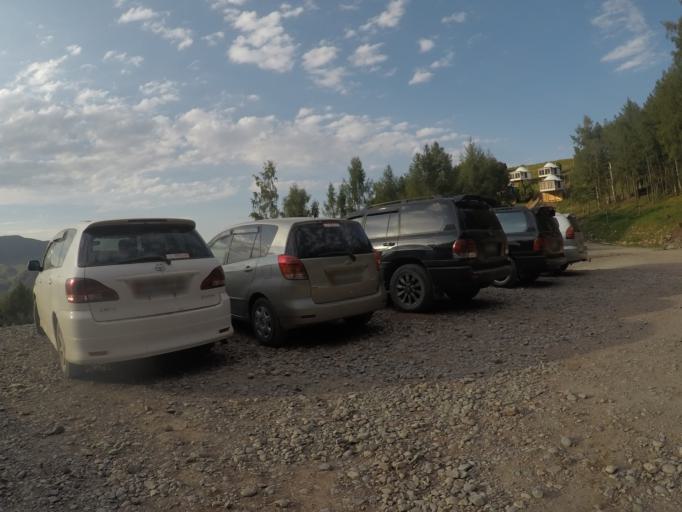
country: KG
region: Chuy
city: Bishkek
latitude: 42.6291
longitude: 74.6214
